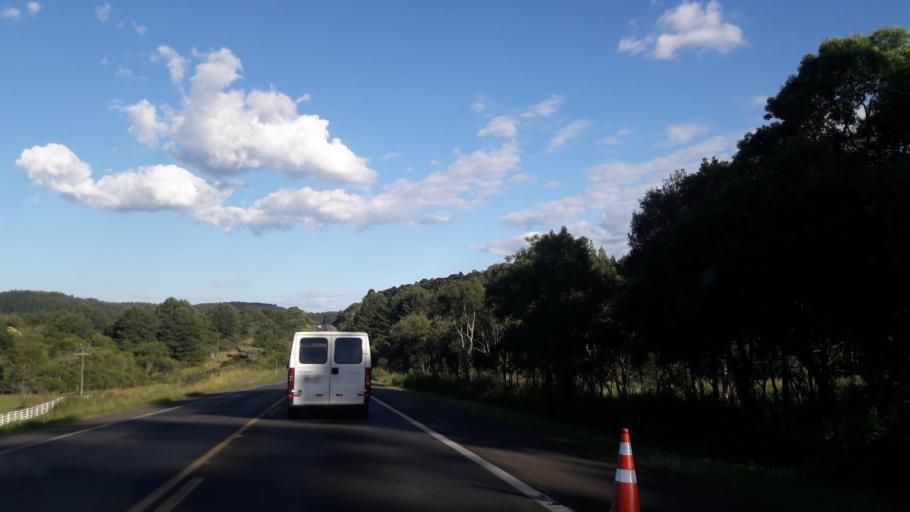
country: BR
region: Parana
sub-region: Guarapuava
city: Guarapuava
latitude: -25.3678
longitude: -51.3342
